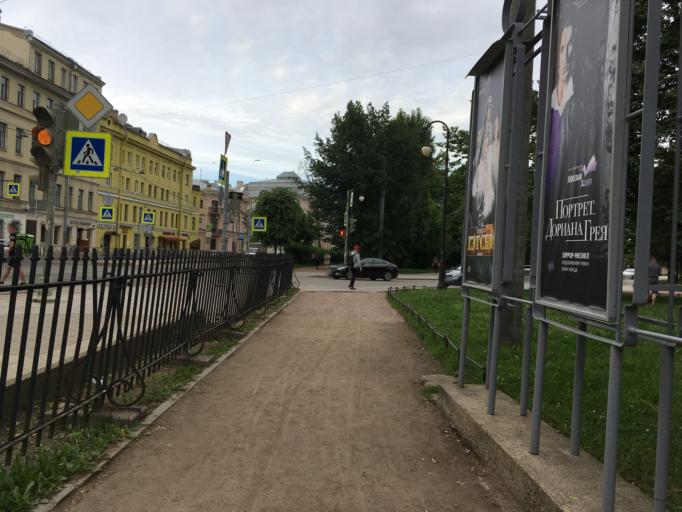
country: RU
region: St.-Petersburg
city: Petrogradka
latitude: 59.9547
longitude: 30.3078
